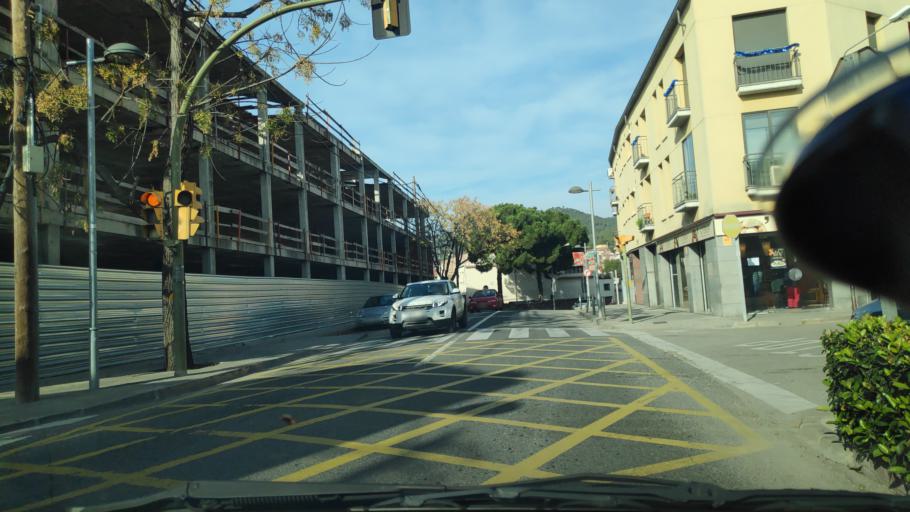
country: ES
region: Catalonia
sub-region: Provincia de Barcelona
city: Castellar del Valles
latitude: 41.6139
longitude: 2.0829
